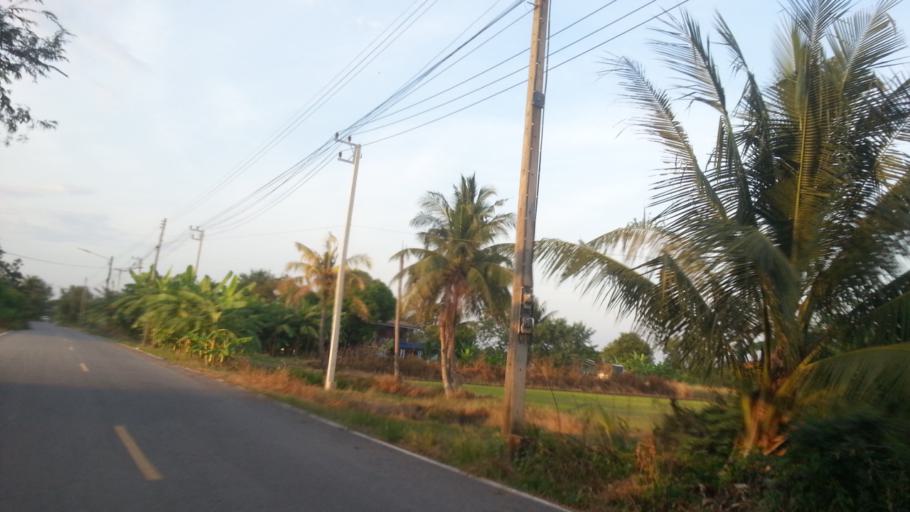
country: TH
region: Pathum Thani
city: Ban Rangsit
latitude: 14.0421
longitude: 100.8476
